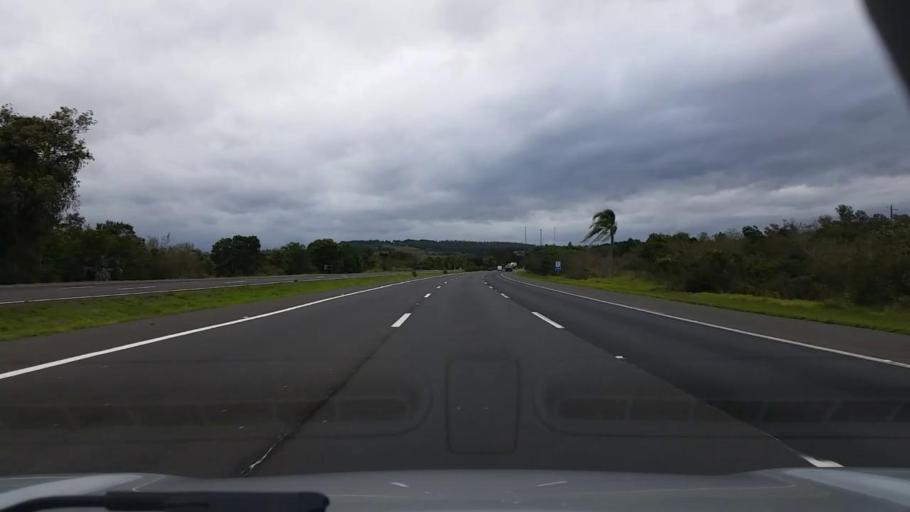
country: BR
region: Rio Grande do Sul
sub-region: Osorio
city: Osorio
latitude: -29.8893
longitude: -50.4604
